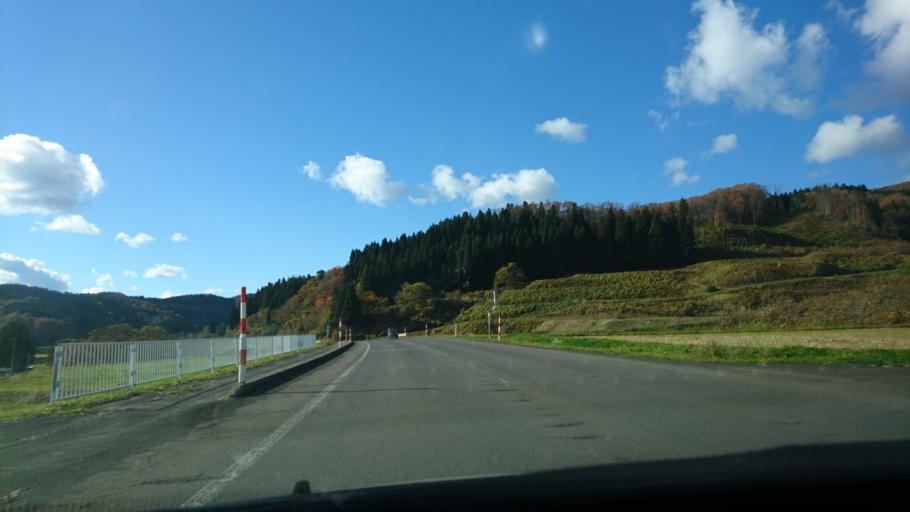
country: JP
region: Akita
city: Omagari
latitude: 39.3145
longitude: 140.2275
